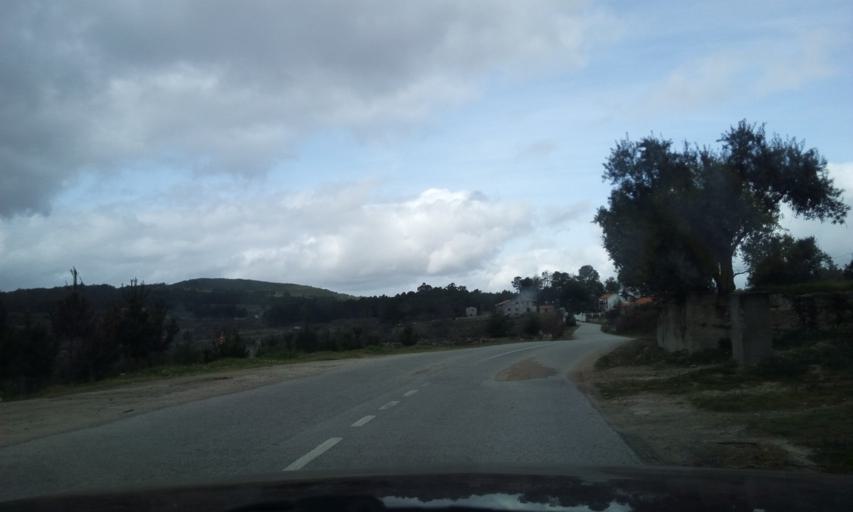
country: PT
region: Guarda
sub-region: Fornos de Algodres
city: Fornos de Algodres
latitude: 40.6602
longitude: -7.5958
